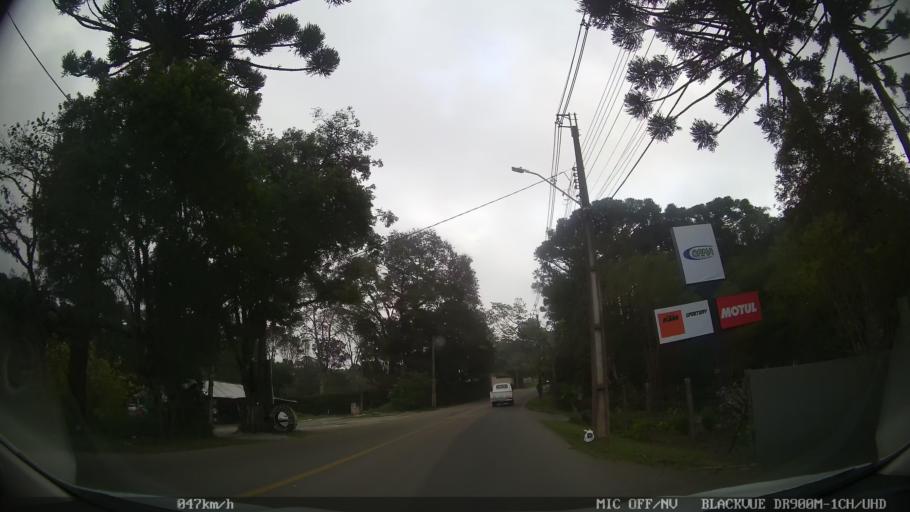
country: BR
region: Parana
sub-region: Almirante Tamandare
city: Almirante Tamandare
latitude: -25.3713
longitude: -49.3214
